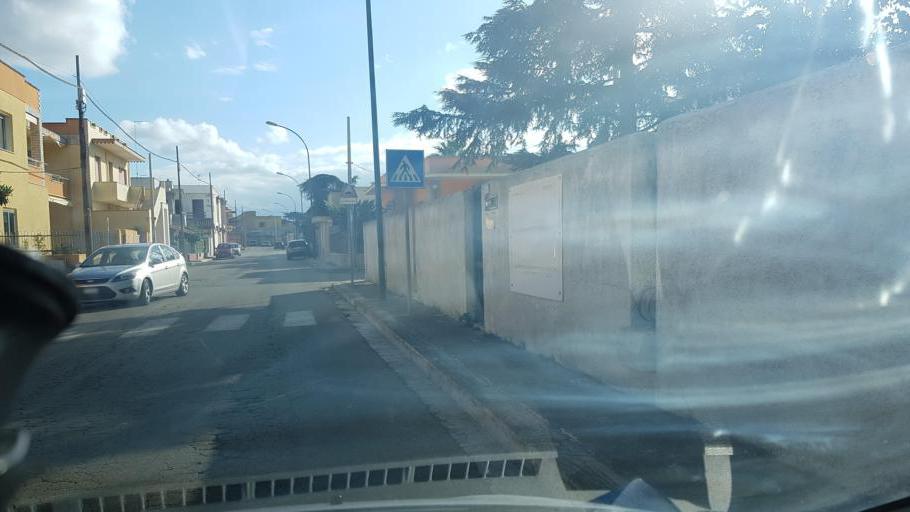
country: IT
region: Apulia
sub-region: Provincia di Lecce
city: Squinzano
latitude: 40.4340
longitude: 18.0316
